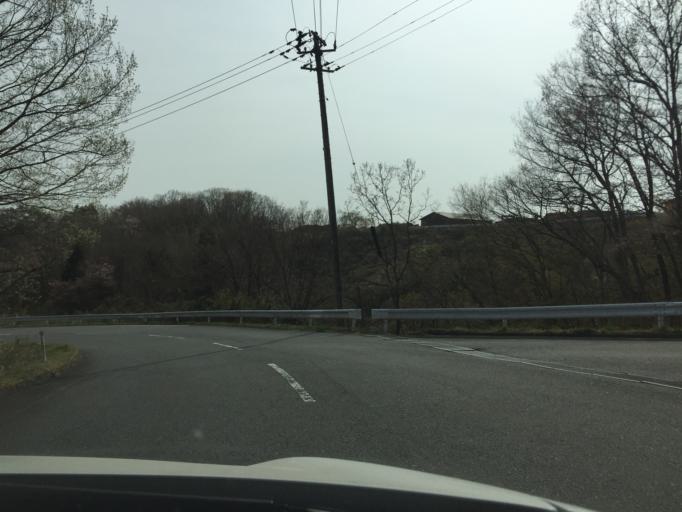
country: JP
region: Fukushima
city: Iwaki
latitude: 37.0218
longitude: 140.7630
